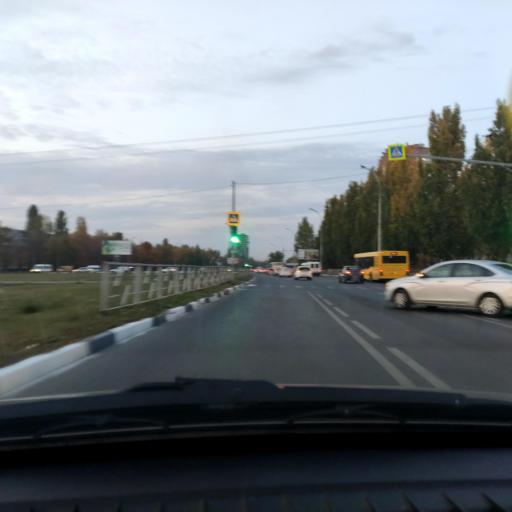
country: RU
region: Samara
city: Tol'yatti
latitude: 53.5188
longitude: 49.2954
